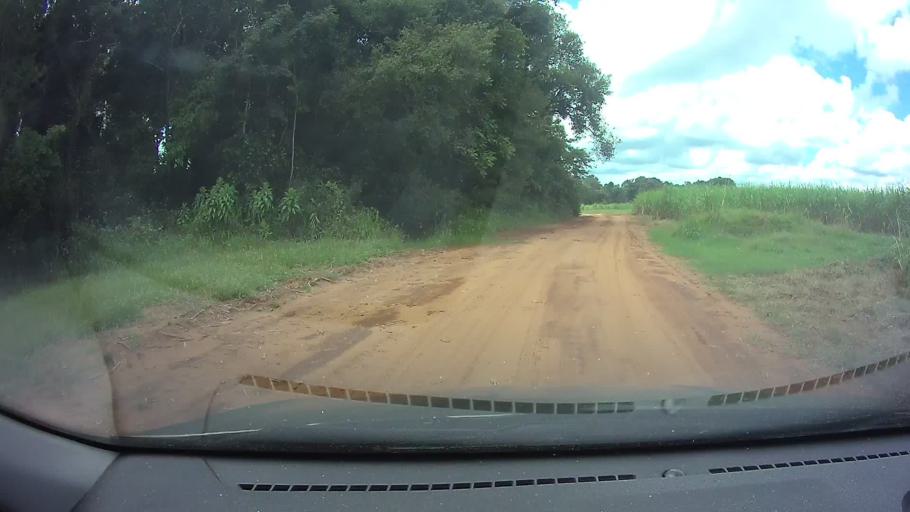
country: PY
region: Paraguari
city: La Colmena
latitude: -25.9508
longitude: -56.7785
